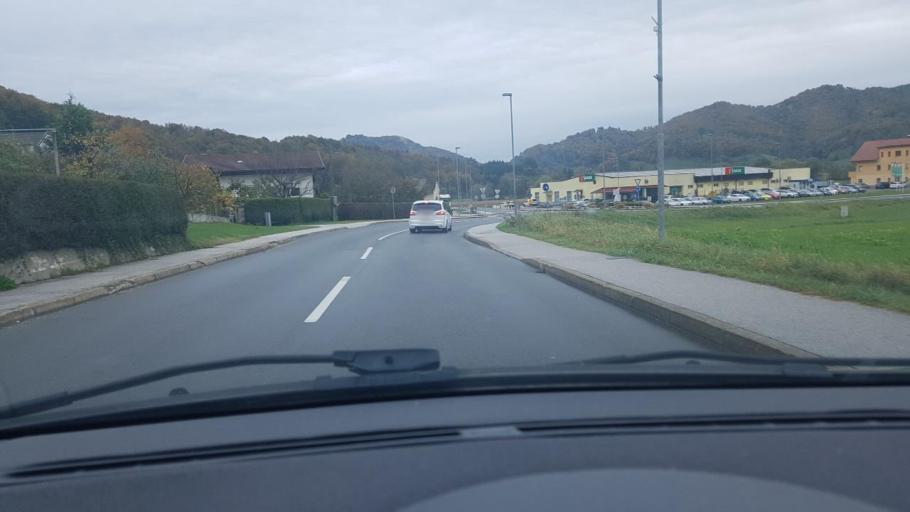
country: SI
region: Majsperk
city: Majsperk
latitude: 46.3488
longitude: 15.7383
